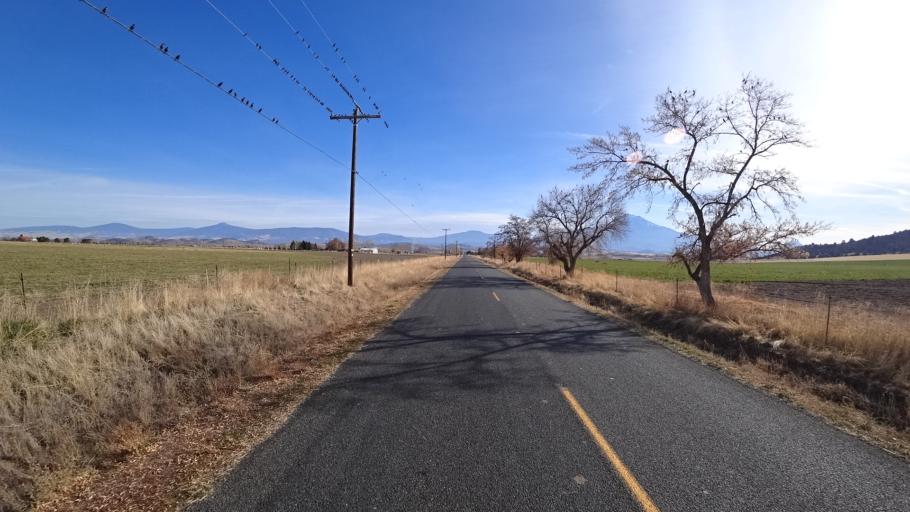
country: US
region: California
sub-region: Siskiyou County
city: Montague
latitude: 41.5381
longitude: -122.5578
